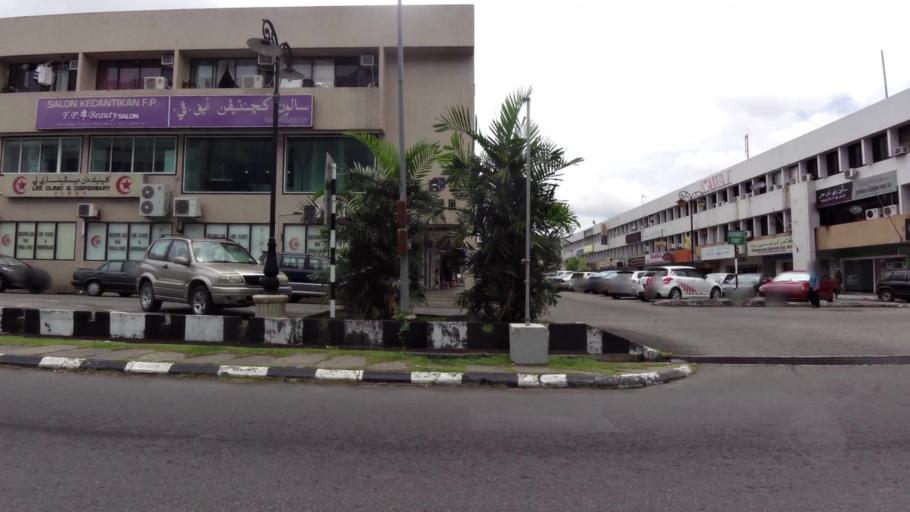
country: BN
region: Brunei and Muara
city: Bandar Seri Begawan
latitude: 4.9076
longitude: 114.9159
